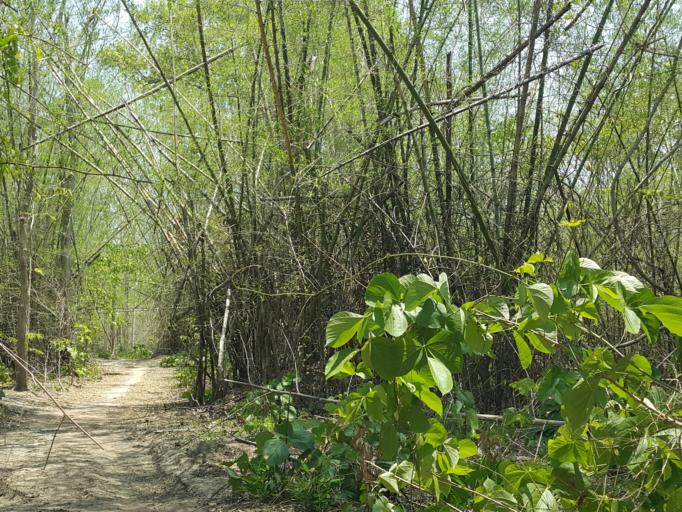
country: TH
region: Kanchanaburi
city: Sai Yok
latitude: 14.2209
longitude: 98.8810
